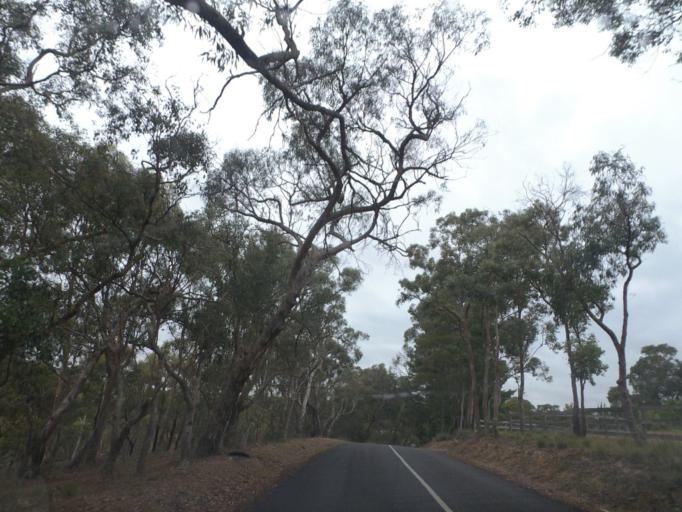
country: AU
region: Victoria
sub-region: Nillumbik
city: Saint Andrews
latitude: -37.6275
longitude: 145.2731
